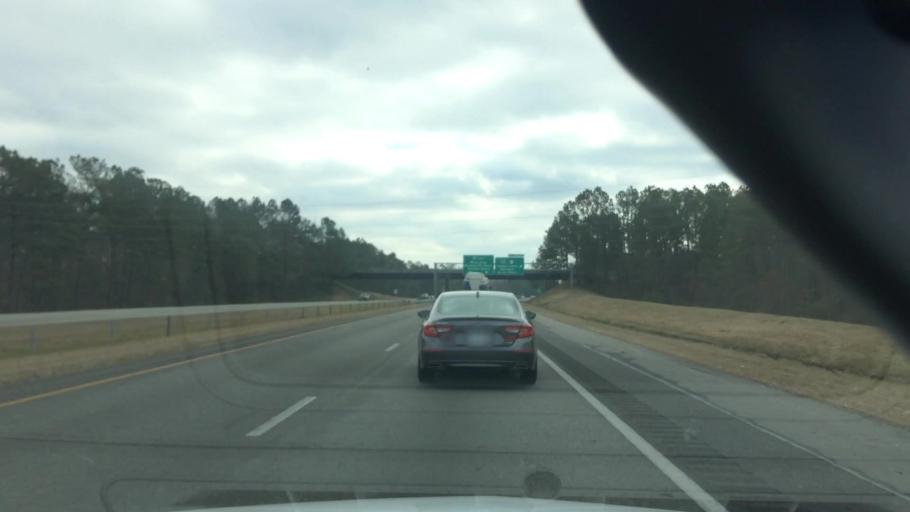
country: US
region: North Carolina
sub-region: New Hanover County
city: Skippers Corner
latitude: 34.3293
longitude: -77.8741
